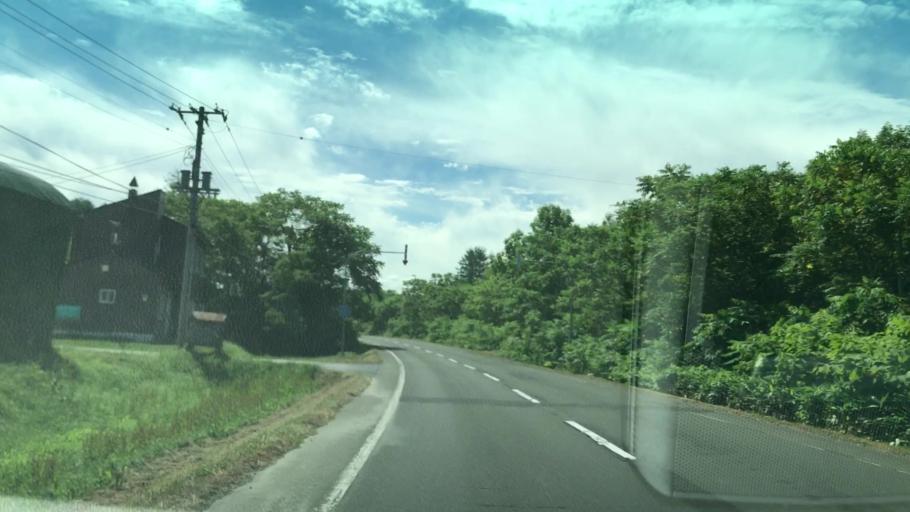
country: JP
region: Hokkaido
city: Shimo-furano
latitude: 42.9588
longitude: 142.4287
